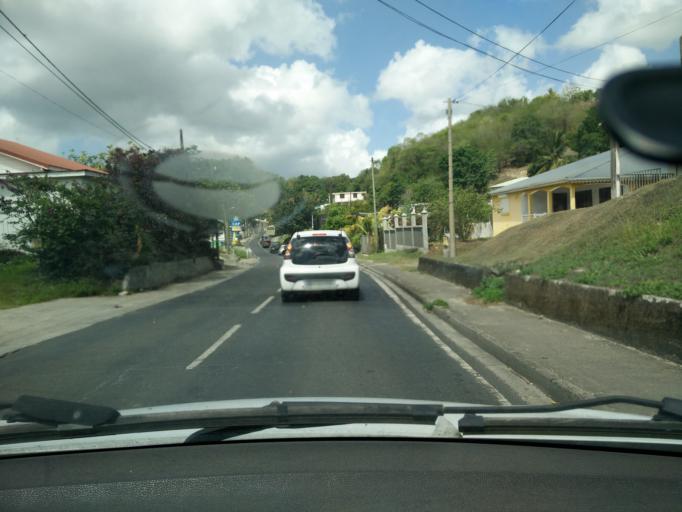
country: GP
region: Guadeloupe
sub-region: Guadeloupe
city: Les Abymes
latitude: 16.2658
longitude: -61.4866
